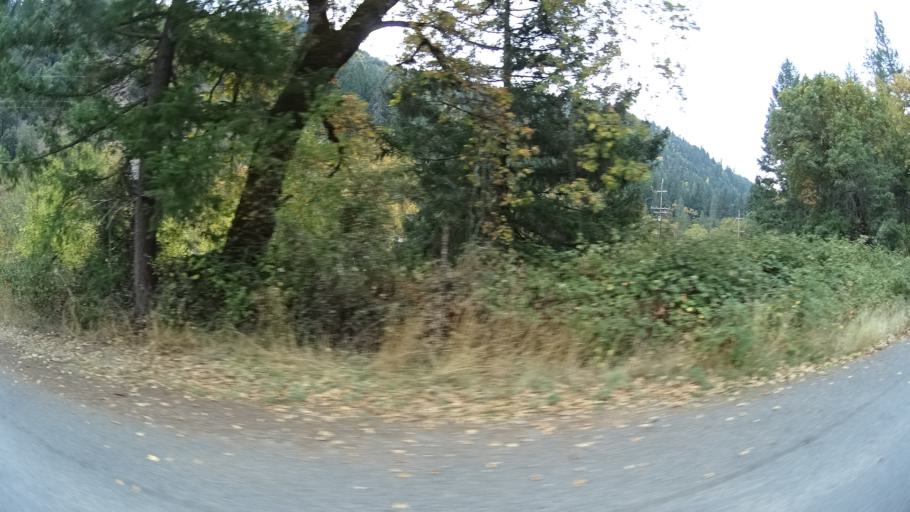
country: US
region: California
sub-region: Siskiyou County
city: Happy Camp
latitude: 41.8262
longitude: -123.3830
